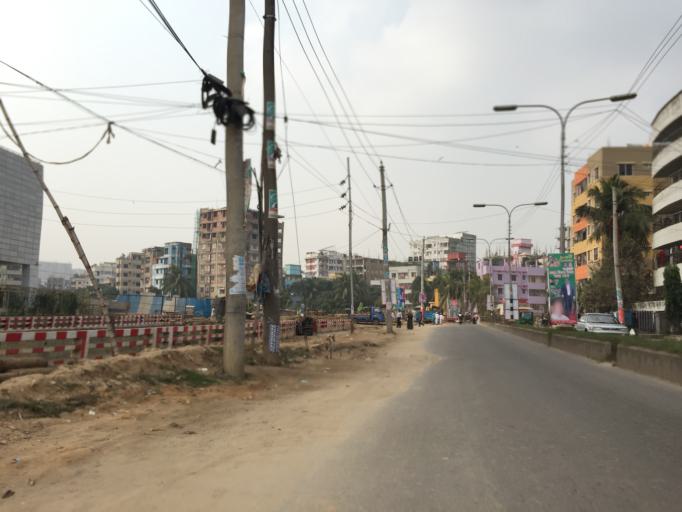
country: BD
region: Dhaka
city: Azimpur
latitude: 23.7786
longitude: 90.3687
